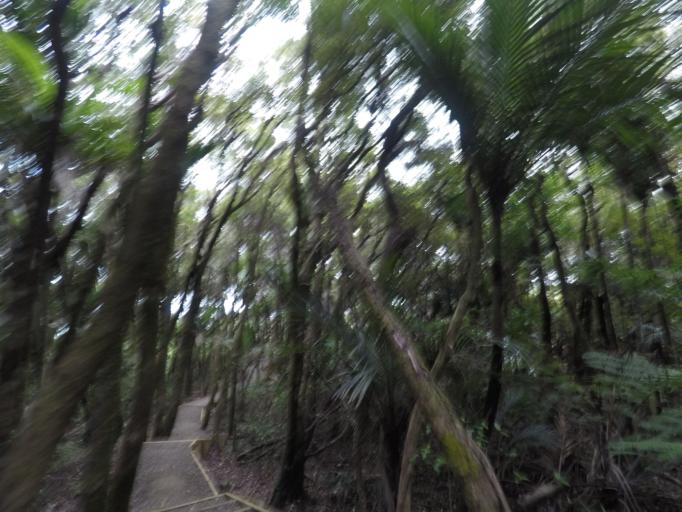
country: NZ
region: Auckland
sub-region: Auckland
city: Titirangi
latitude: -37.0287
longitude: 174.5278
